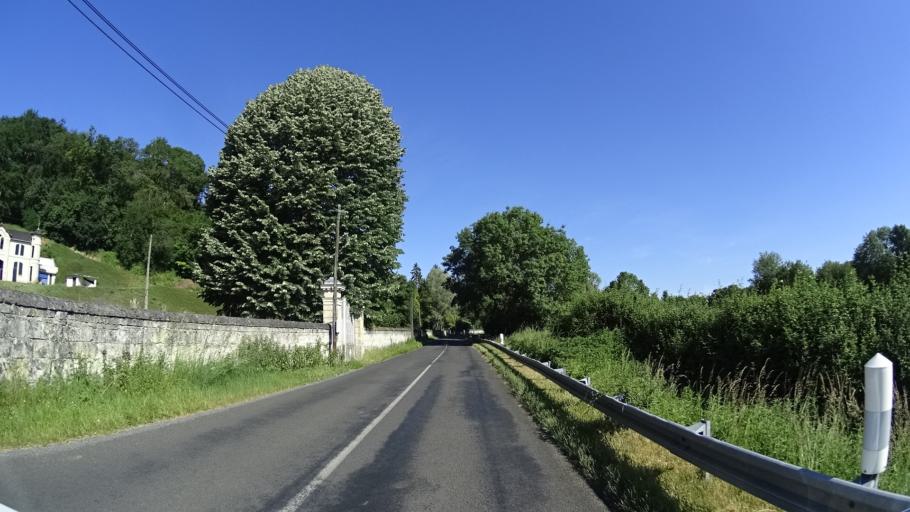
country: FR
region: Pays de la Loire
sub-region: Departement de Maine-et-Loire
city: Saint-Martin-de-la-Place
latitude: 47.2905
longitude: -0.1345
